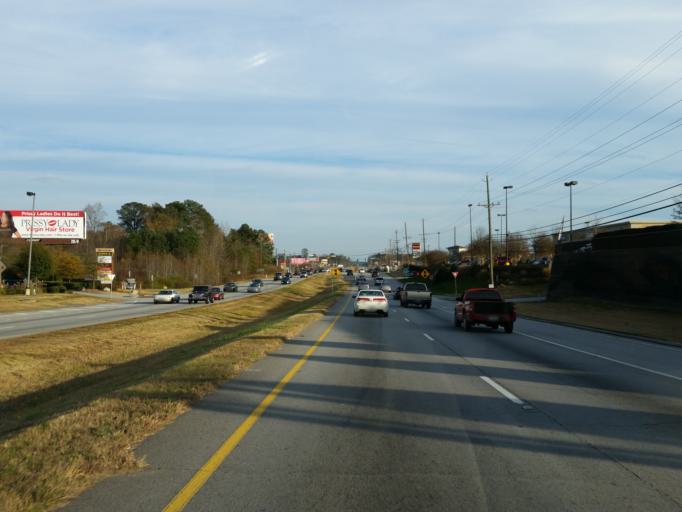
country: US
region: Georgia
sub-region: Paulding County
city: Hiram
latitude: 33.8879
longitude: -84.7439
